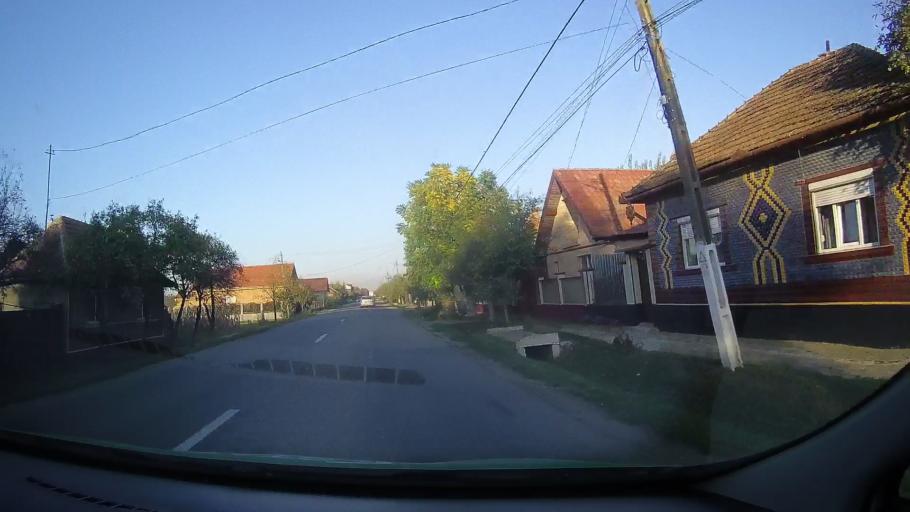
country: RO
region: Bihor
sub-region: Comuna Salard
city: Salard
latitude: 47.2129
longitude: 22.0254
